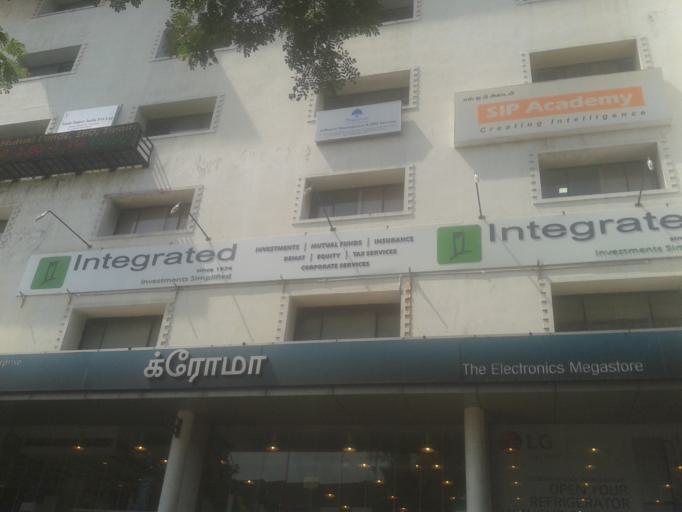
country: IN
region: Tamil Nadu
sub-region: Chennai
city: Chetput
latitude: 13.0482
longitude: 80.2349
